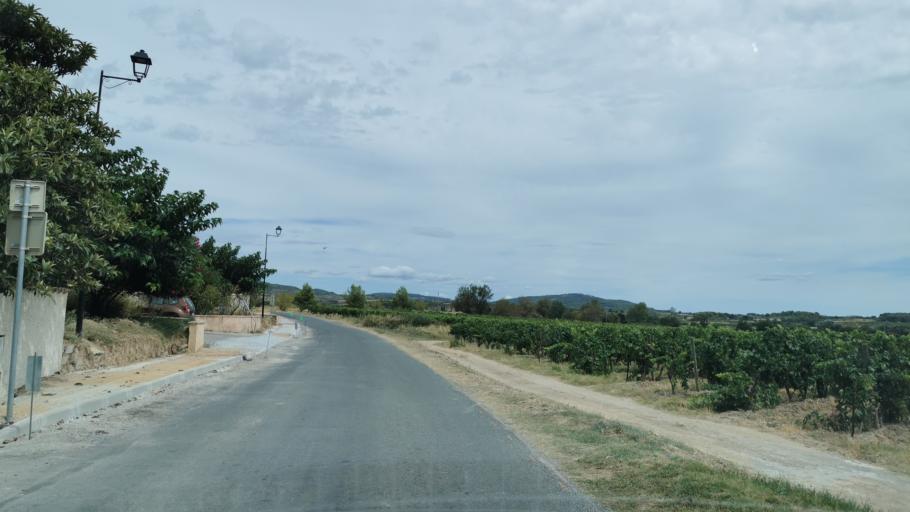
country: FR
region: Languedoc-Roussillon
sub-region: Departement de l'Aude
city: Ginestas
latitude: 43.2893
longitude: 2.8244
